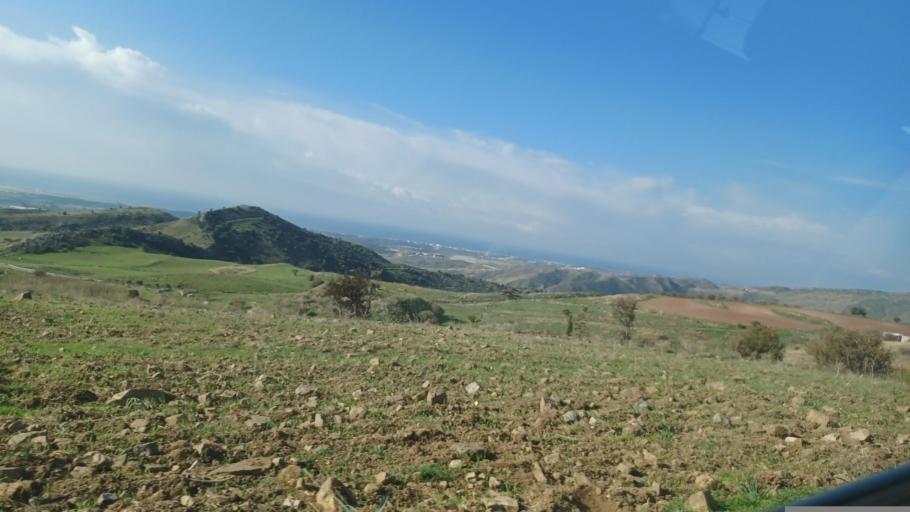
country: CY
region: Pafos
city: Mesogi
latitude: 34.7752
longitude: 32.5426
